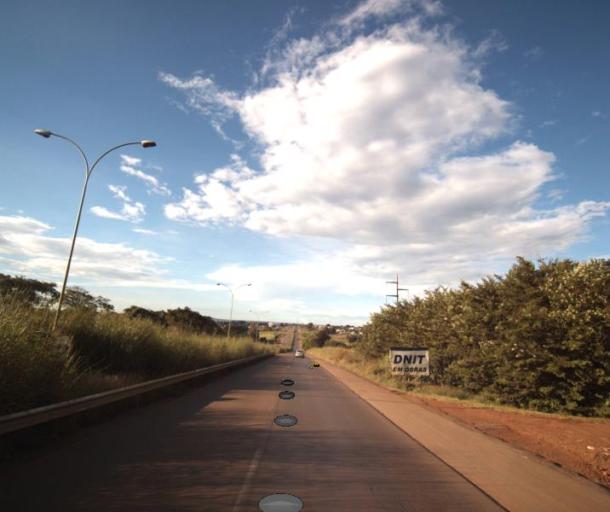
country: BR
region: Goias
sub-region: Anapolis
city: Anapolis
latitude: -16.3513
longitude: -48.9280
